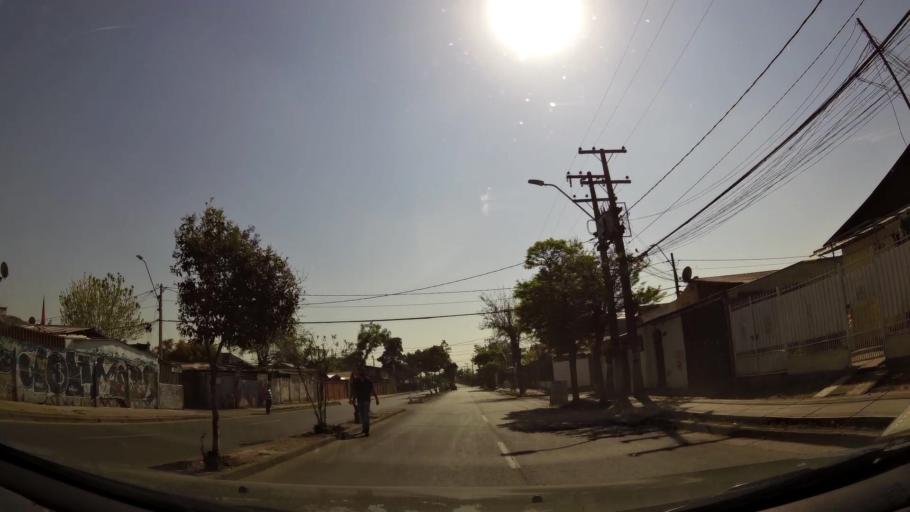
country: CL
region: Santiago Metropolitan
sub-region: Provincia de Maipo
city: San Bernardo
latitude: -33.5906
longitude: -70.6891
